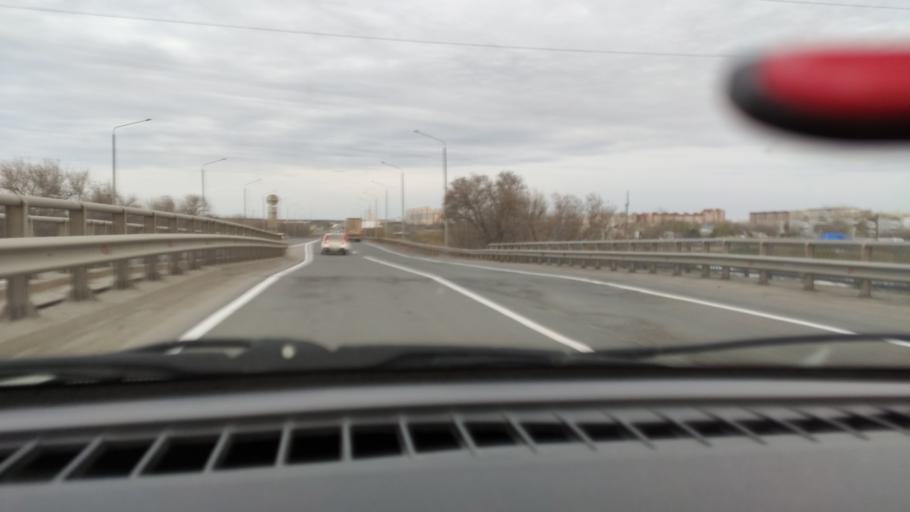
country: RU
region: Orenburg
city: Orenburg
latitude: 51.8518
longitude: 55.1407
